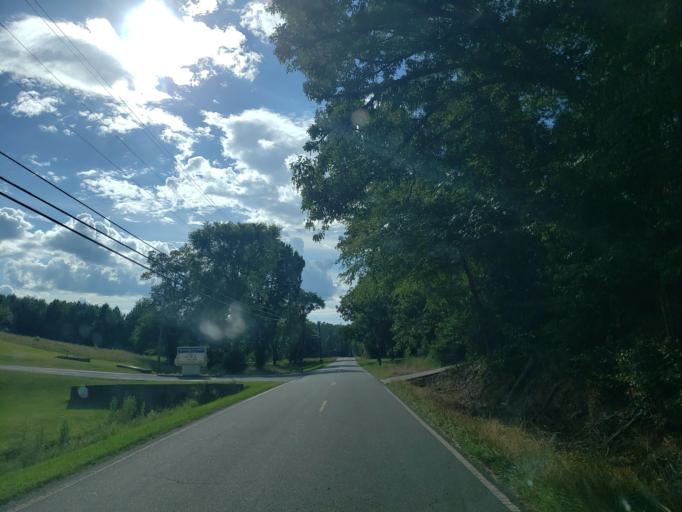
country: US
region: Georgia
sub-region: Floyd County
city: Lindale
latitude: 34.2011
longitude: -85.0899
